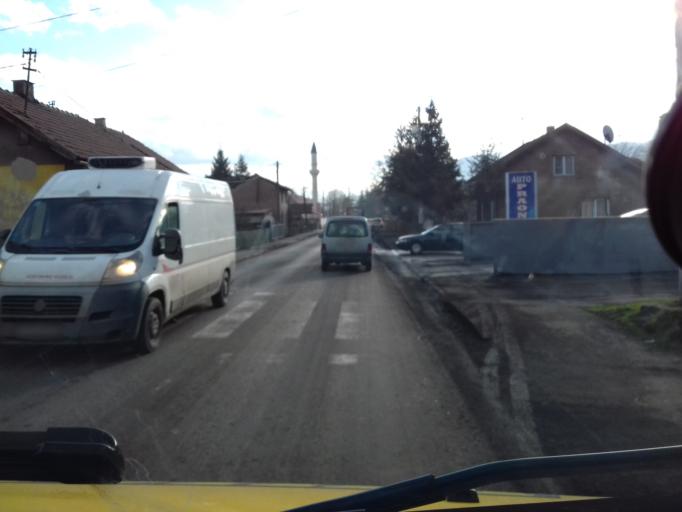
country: BA
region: Federation of Bosnia and Herzegovina
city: Zenica
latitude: 44.2047
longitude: 17.8989
